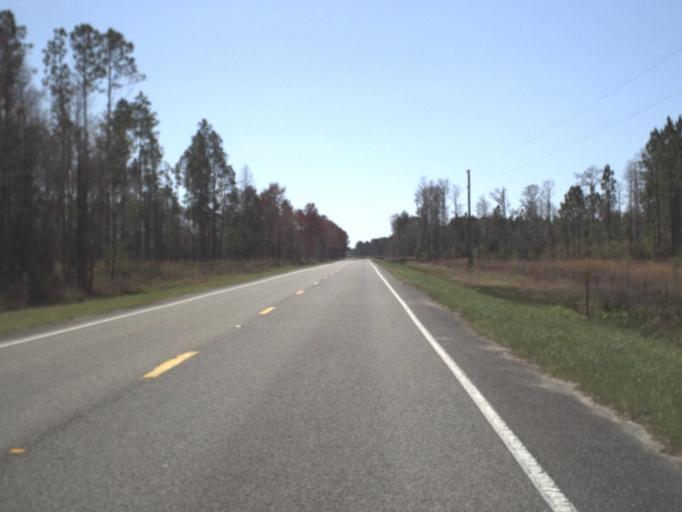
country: US
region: Florida
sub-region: Leon County
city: Woodville
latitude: 30.2582
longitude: -84.0425
